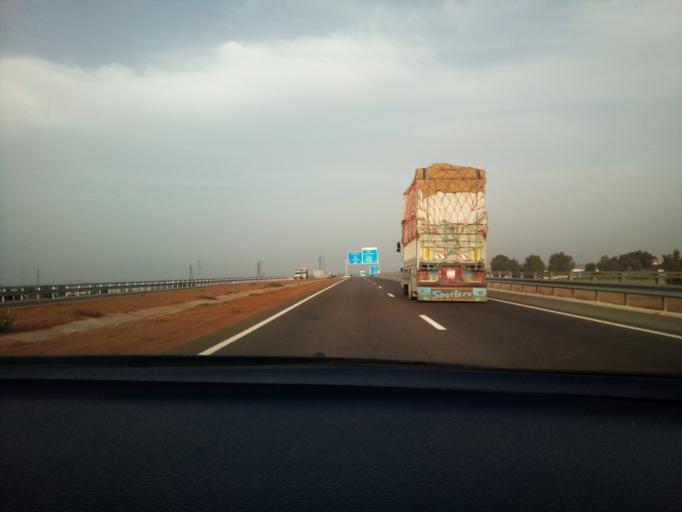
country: MA
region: Rabat-Sale-Zemmour-Zaer
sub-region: Skhirate-Temara
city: Temara
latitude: 33.8428
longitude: -6.8482
